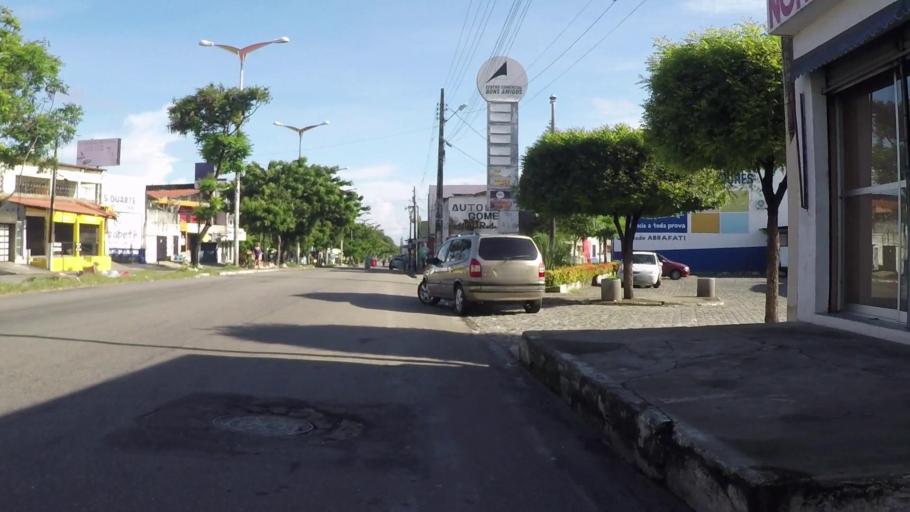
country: BR
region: Ceara
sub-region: Fortaleza
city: Fortaleza
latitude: -3.7278
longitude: -38.5851
